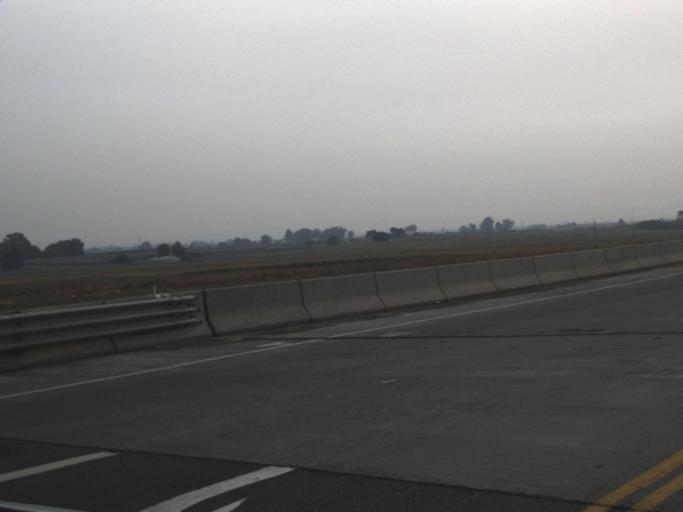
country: US
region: Washington
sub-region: Yakima County
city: Sunnyside
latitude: 46.3068
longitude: -119.9785
